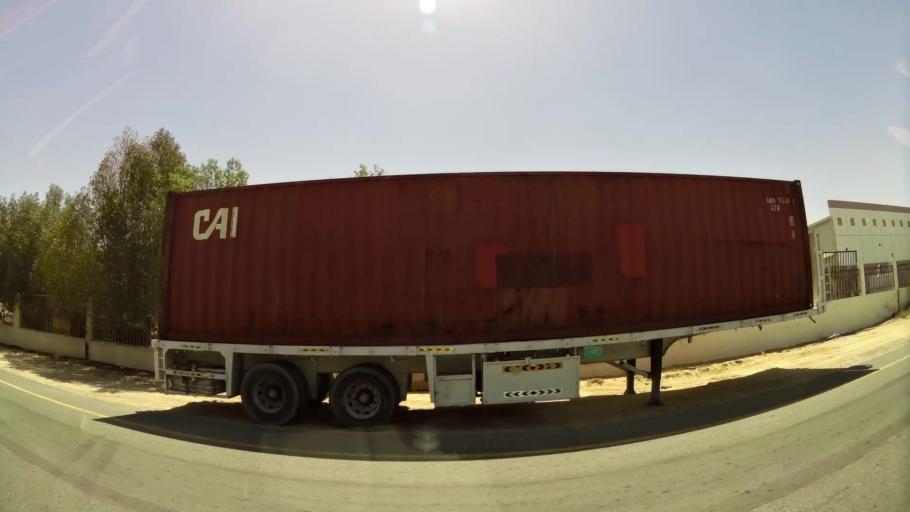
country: AE
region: Dubai
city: Dubai
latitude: 24.9870
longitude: 55.2072
